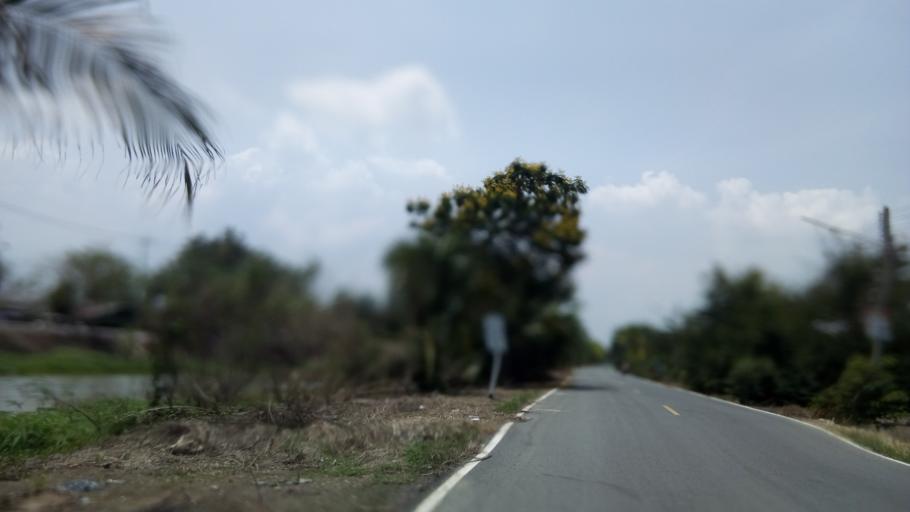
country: TH
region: Pathum Thani
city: Nong Suea
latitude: 14.2065
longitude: 100.8229
